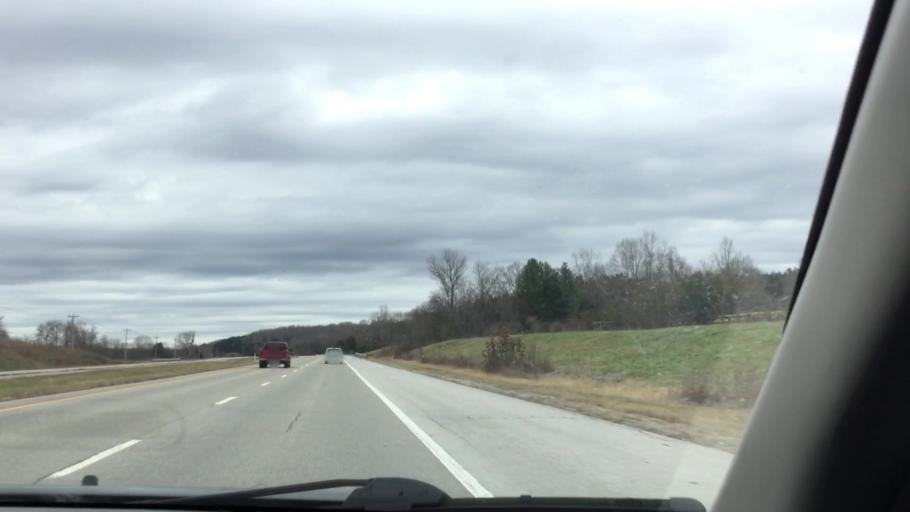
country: US
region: Tennessee
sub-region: Lewis County
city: Hohenwald
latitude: 35.5869
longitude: -87.4469
